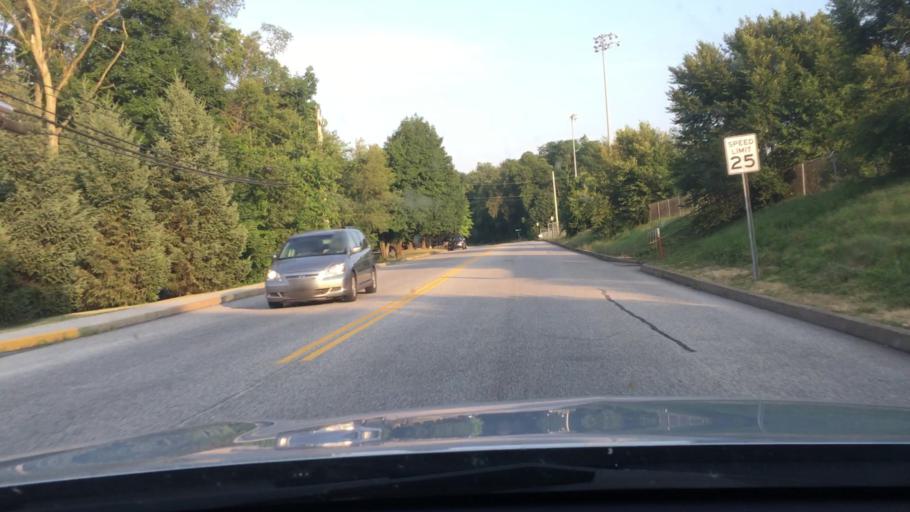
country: US
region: Pennsylvania
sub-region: York County
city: Dillsburg
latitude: 40.1091
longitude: -77.0328
